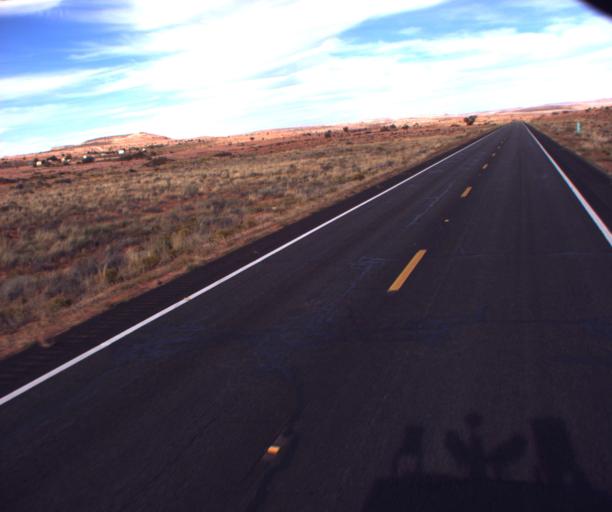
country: US
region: Arizona
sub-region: Navajo County
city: Kayenta
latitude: 36.9339
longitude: -109.7436
